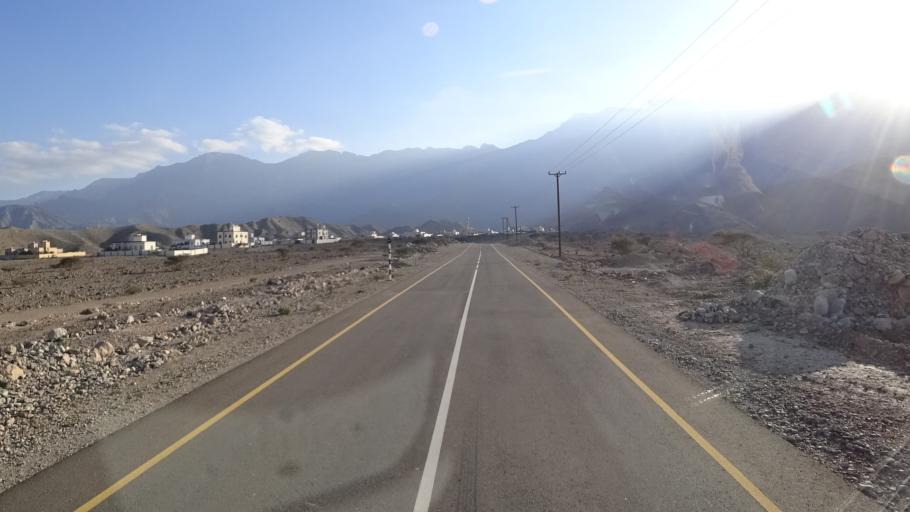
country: OM
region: Al Batinah
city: Rustaq
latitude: 23.2734
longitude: 57.3258
